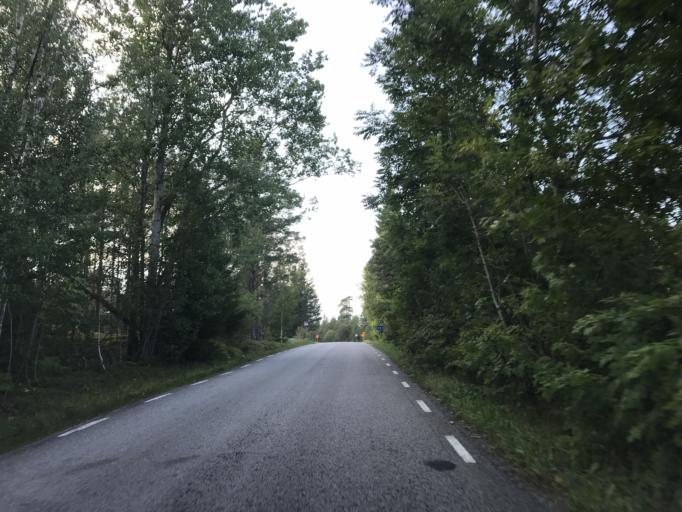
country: SE
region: Stockholm
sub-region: Norrtalje Kommun
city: Bjorko
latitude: 59.8652
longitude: 19.0323
